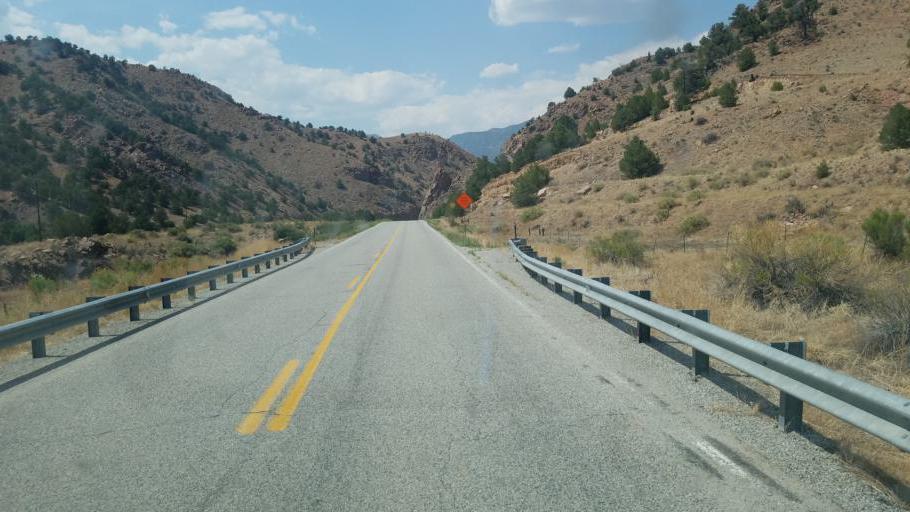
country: US
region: Colorado
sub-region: Custer County
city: Westcliffe
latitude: 38.4010
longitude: -105.5824
